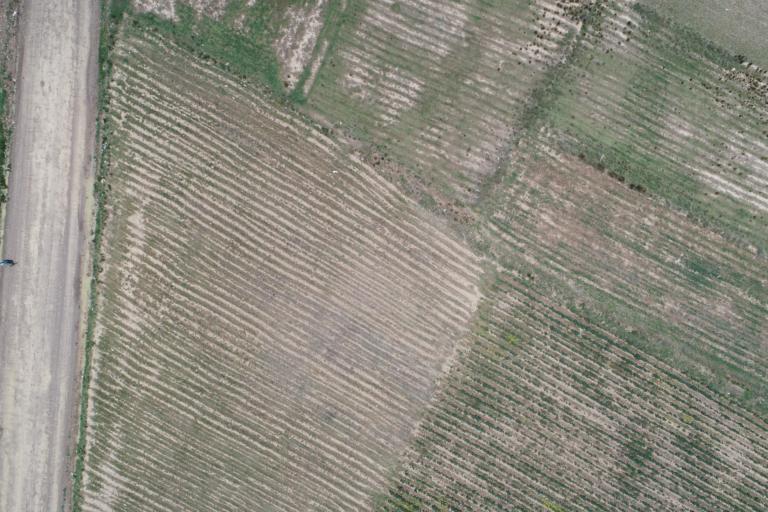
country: BO
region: La Paz
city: Huarina
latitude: -16.1874
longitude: -68.6056
